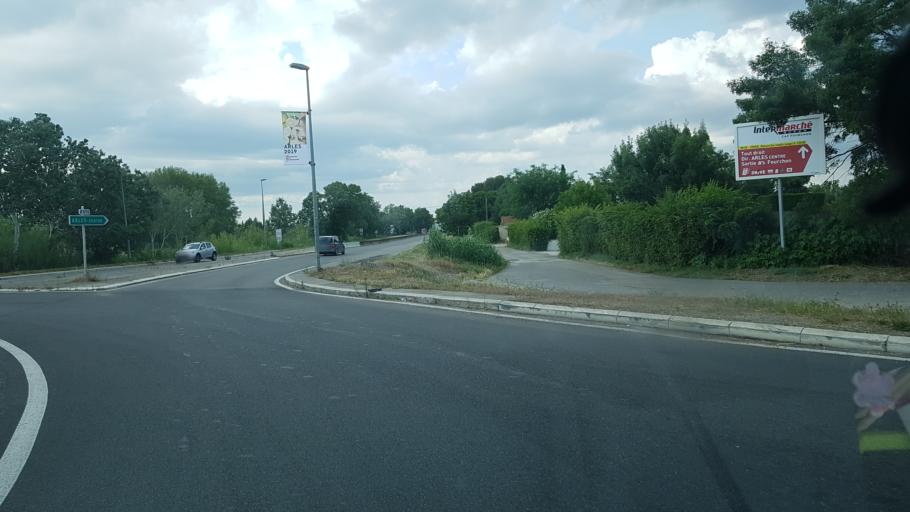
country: FR
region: Languedoc-Roussillon
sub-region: Departement du Gard
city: Fourques
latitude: 43.6734
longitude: 4.6066
